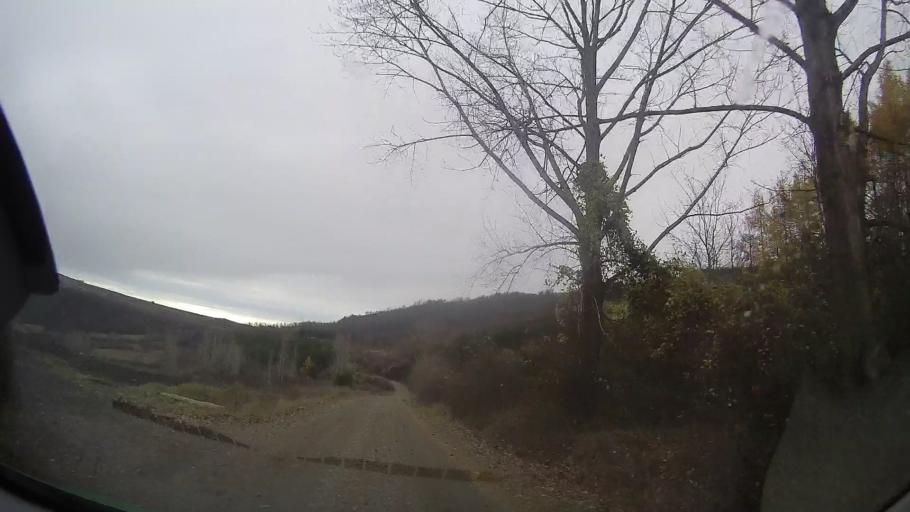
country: RO
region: Mures
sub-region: Comuna Bala
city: Bala
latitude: 46.6784
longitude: 24.4858
